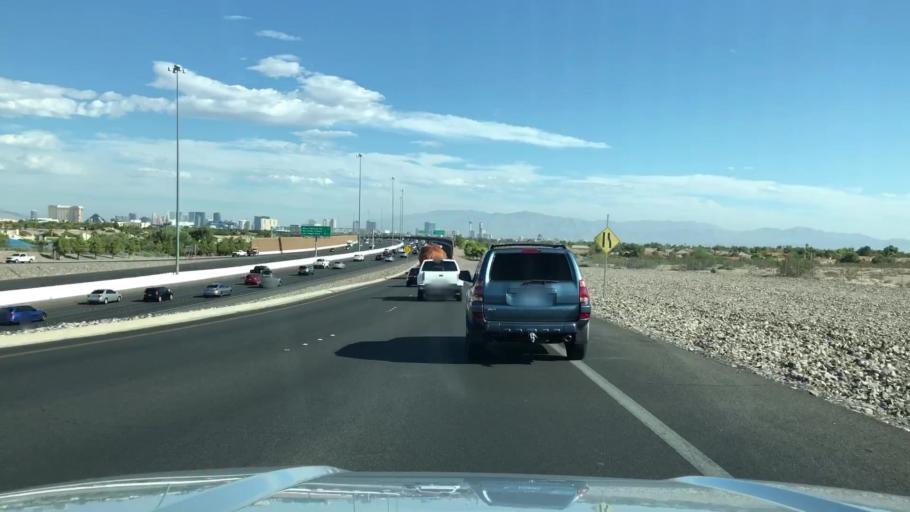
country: US
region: Nevada
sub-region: Clark County
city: Paradise
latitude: 36.0433
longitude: -115.1334
